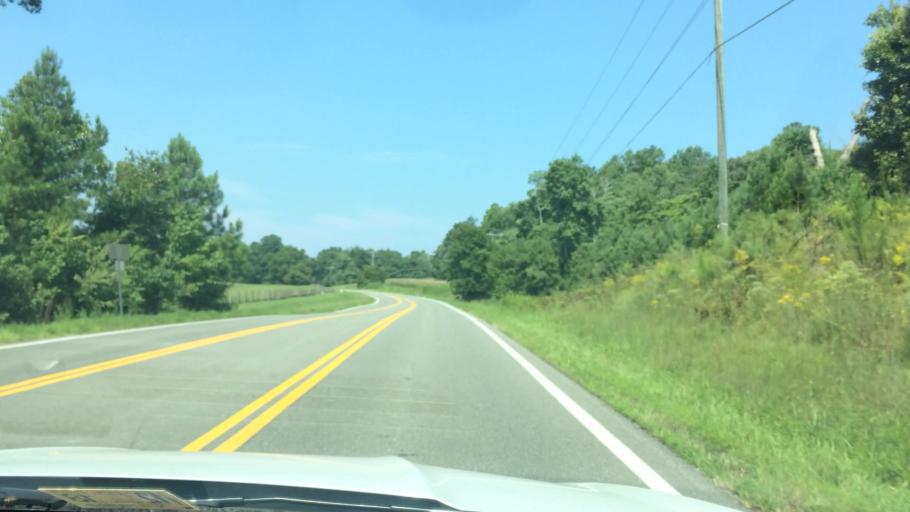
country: US
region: Virginia
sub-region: New Kent County
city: New Kent
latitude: 37.5242
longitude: -77.0100
